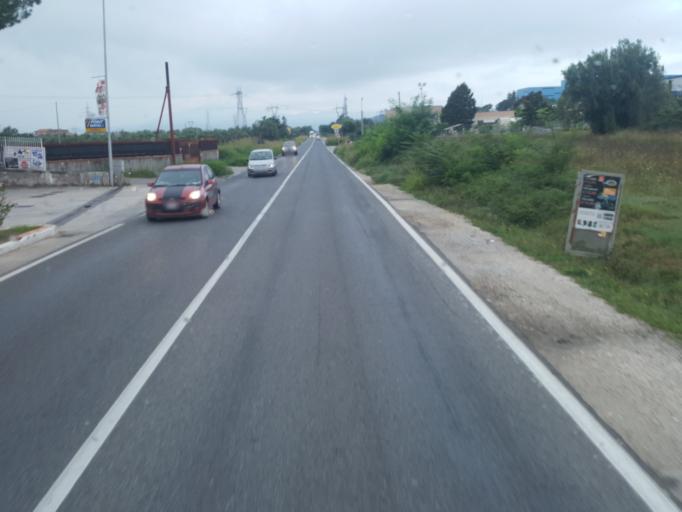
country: IT
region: Campania
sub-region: Provincia di Caserta
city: Sparanise
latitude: 41.1756
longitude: 14.1211
